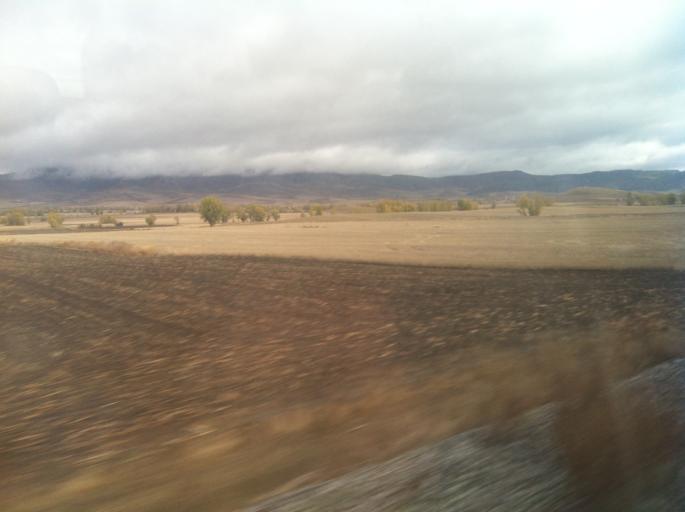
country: ES
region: Castille and Leon
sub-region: Provincia de Burgos
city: Fuentebureba
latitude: 42.6242
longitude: -3.2209
